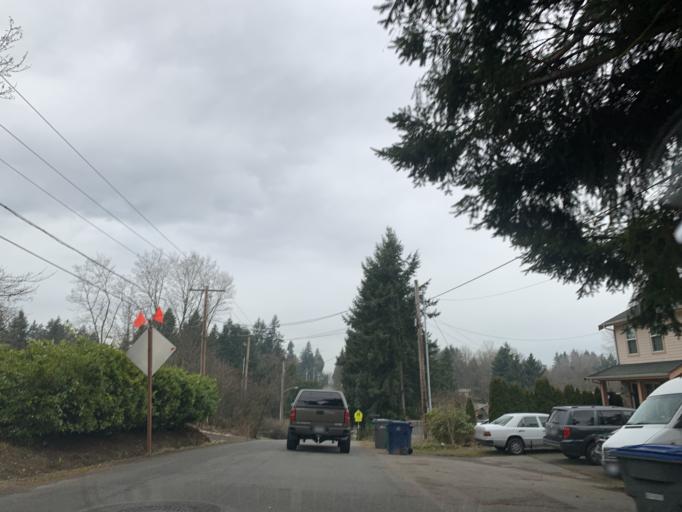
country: US
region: Washington
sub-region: King County
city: Federal Way
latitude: 47.3350
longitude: -122.2979
